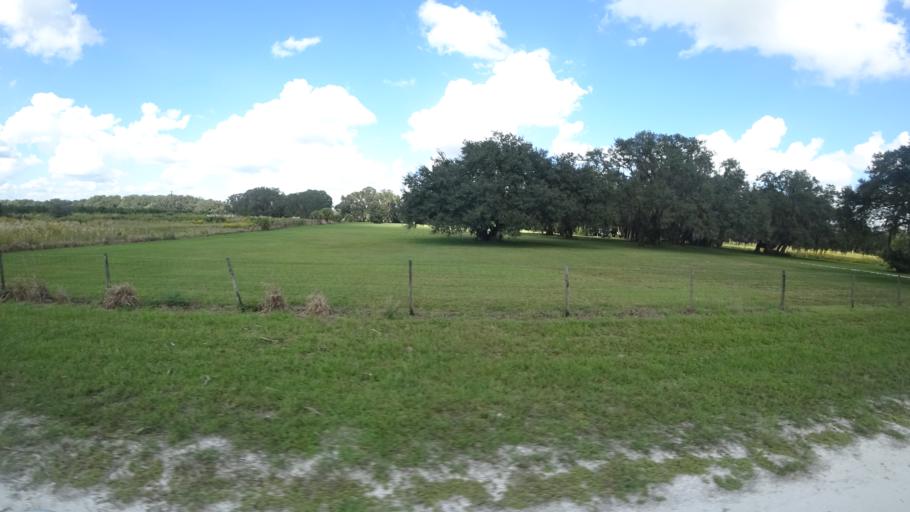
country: US
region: Florida
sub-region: Sarasota County
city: North Port
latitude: 27.2080
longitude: -82.1106
